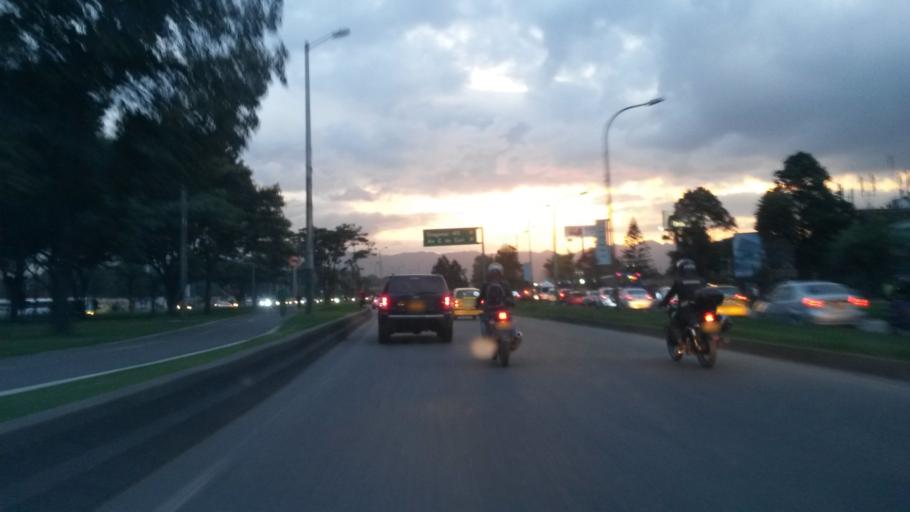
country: CO
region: Cundinamarca
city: Funza
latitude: 4.6869
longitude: -74.1279
